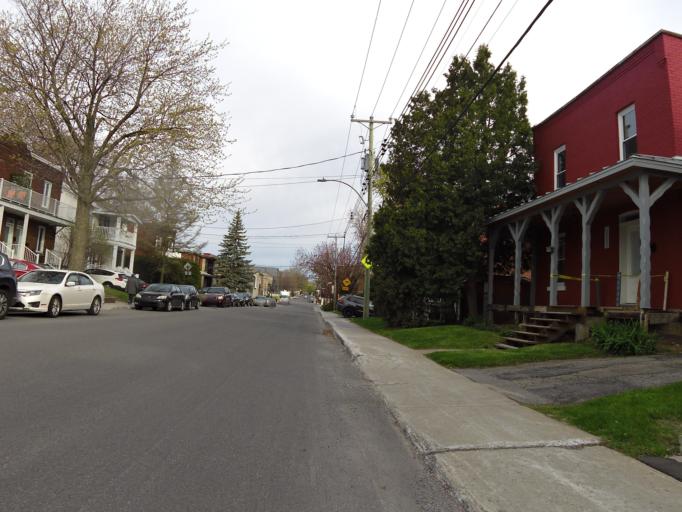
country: CA
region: Quebec
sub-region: Laval
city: Laval
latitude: 45.5422
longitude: -73.6924
